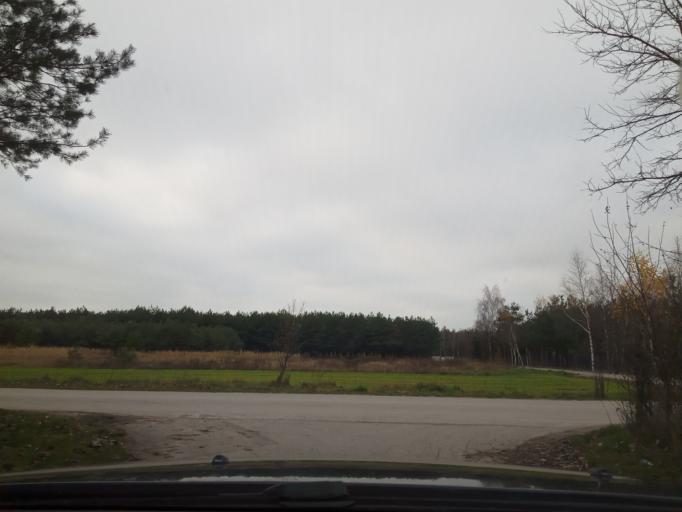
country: PL
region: Swietokrzyskie
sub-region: Powiat jedrzejowski
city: Imielno
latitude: 50.5997
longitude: 20.4851
